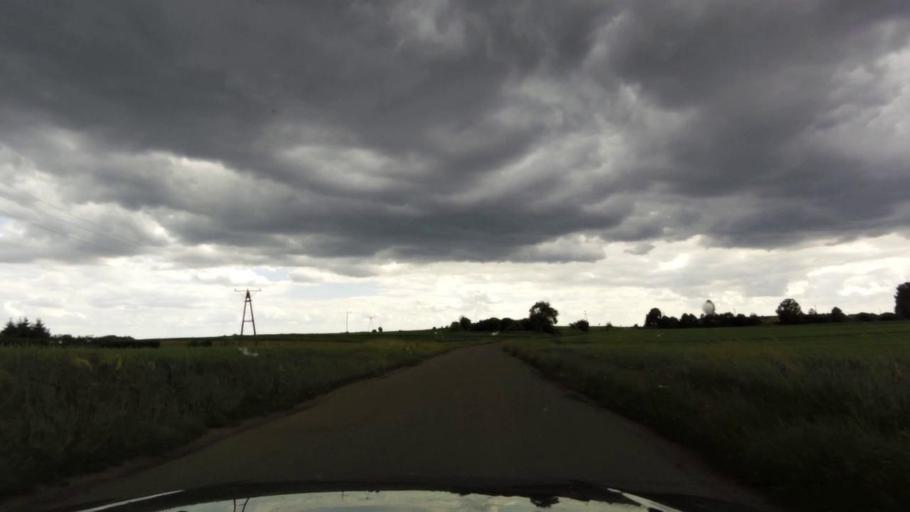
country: PL
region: West Pomeranian Voivodeship
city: Trzcinsko Zdroj
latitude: 52.9585
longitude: 14.6097
